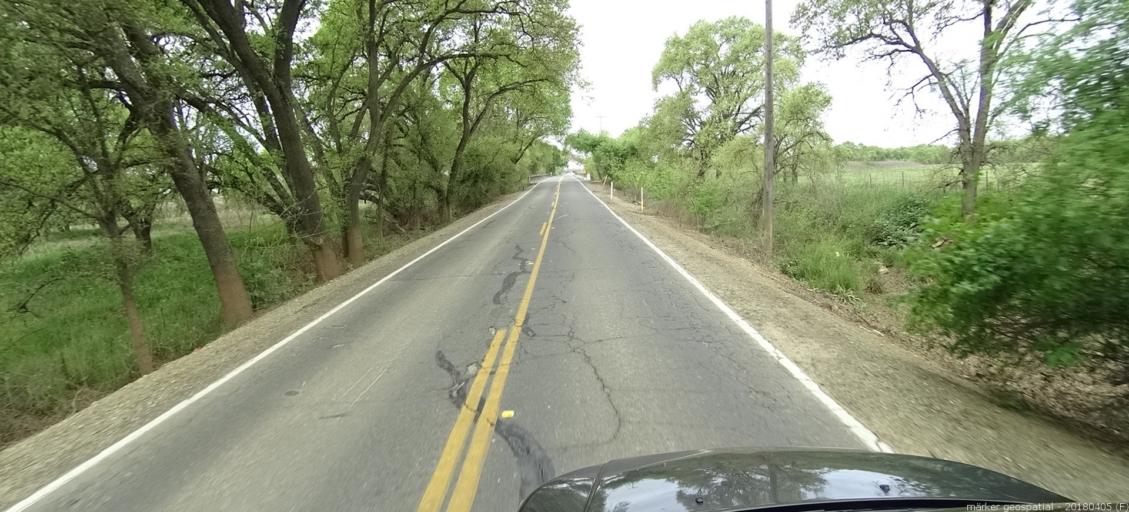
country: US
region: California
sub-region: San Joaquin County
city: Thornton
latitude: 38.2413
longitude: -121.3837
